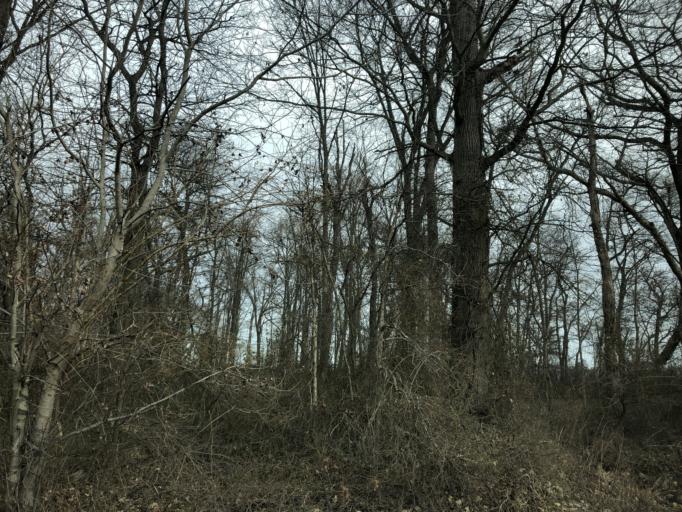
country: US
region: Delaware
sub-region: New Castle County
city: Middletown
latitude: 39.4136
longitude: -75.7612
